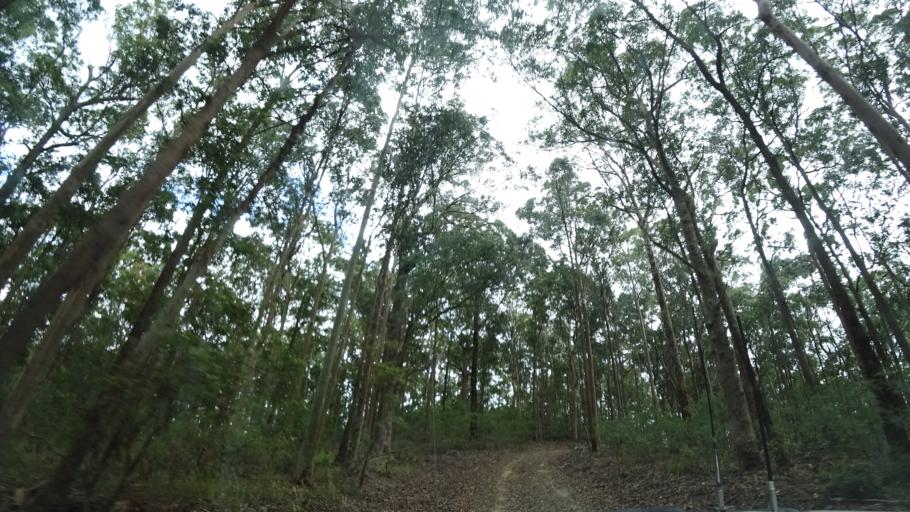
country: AU
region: Queensland
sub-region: Moreton Bay
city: Highvale
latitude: -27.3840
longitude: 152.7534
